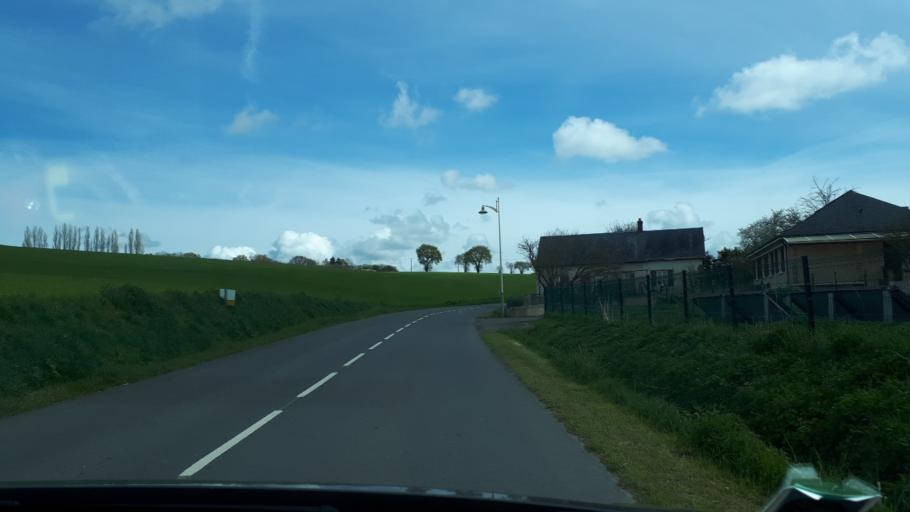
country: FR
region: Pays de la Loire
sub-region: Departement de la Sarthe
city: Le Grand-Luce
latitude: 47.8671
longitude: 0.4861
